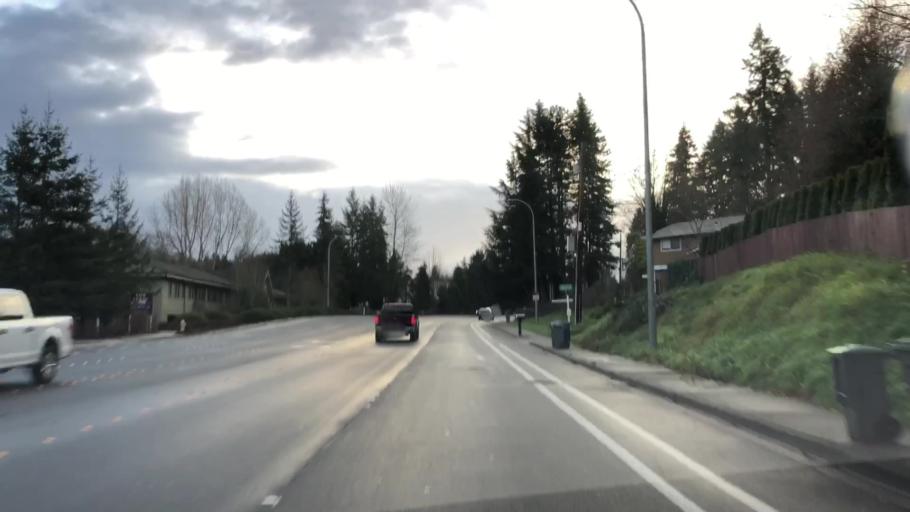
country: US
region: Washington
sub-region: King County
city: Newport
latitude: 47.5947
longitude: -122.1661
